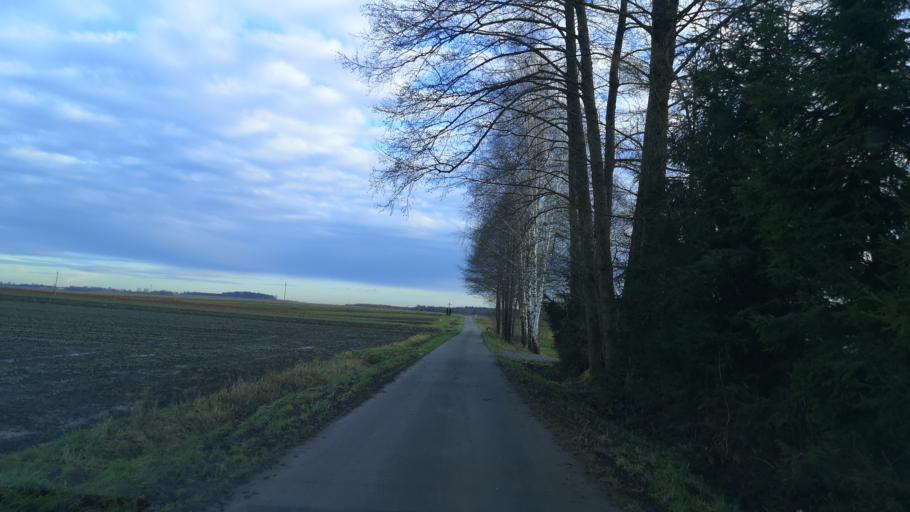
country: PL
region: Subcarpathian Voivodeship
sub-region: Powiat lezajski
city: Piskorowice
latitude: 50.2510
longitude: 22.5777
